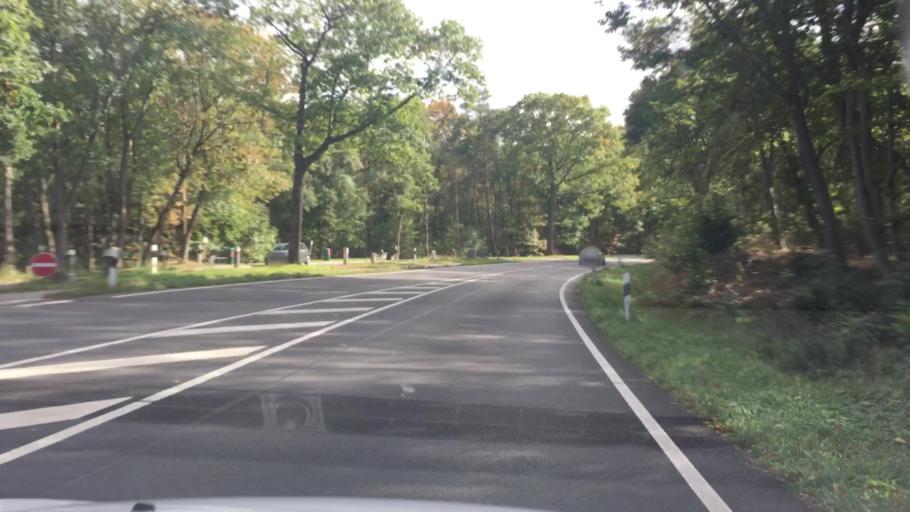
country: DE
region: Lower Saxony
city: Diepholz
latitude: 52.6545
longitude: 8.3356
